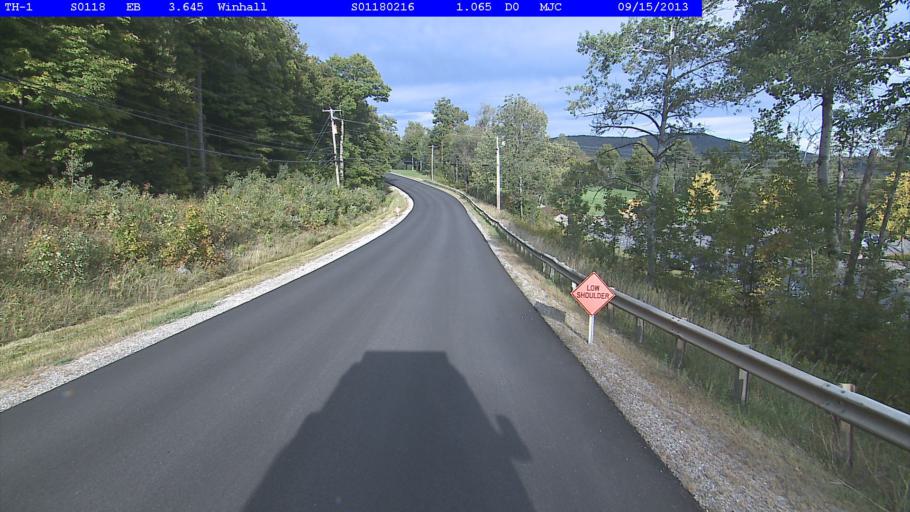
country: US
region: Vermont
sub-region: Bennington County
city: Manchester Center
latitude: 43.1259
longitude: -72.9051
